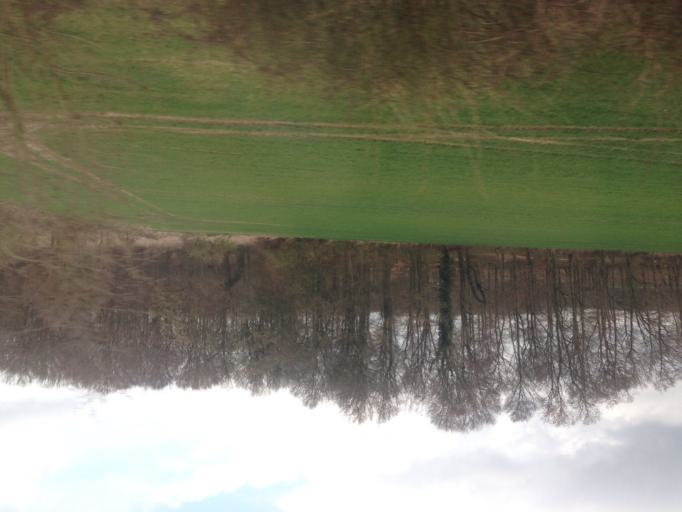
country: DE
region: North Rhine-Westphalia
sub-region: Regierungsbezirk Munster
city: Dulmen
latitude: 51.8429
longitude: 7.3252
